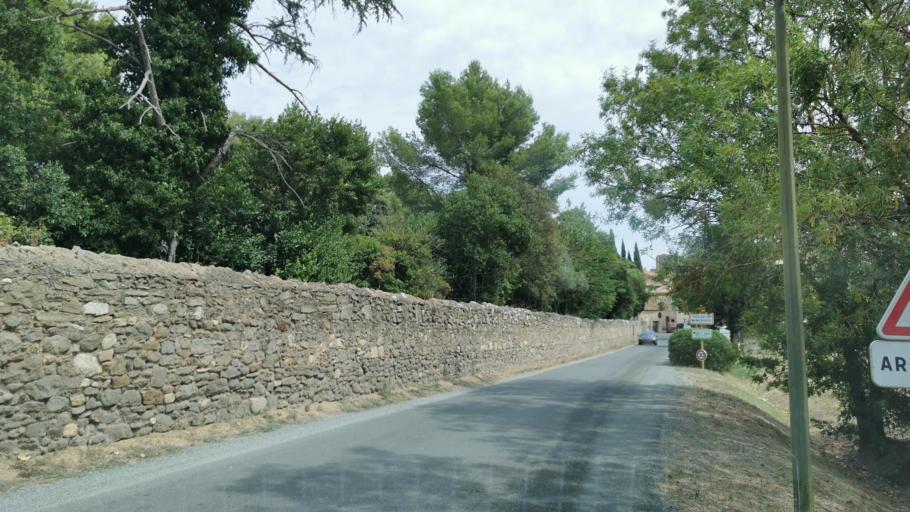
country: FR
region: Languedoc-Roussillon
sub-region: Departement de l'Aude
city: Ginestas
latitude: 43.2867
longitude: 2.8226
